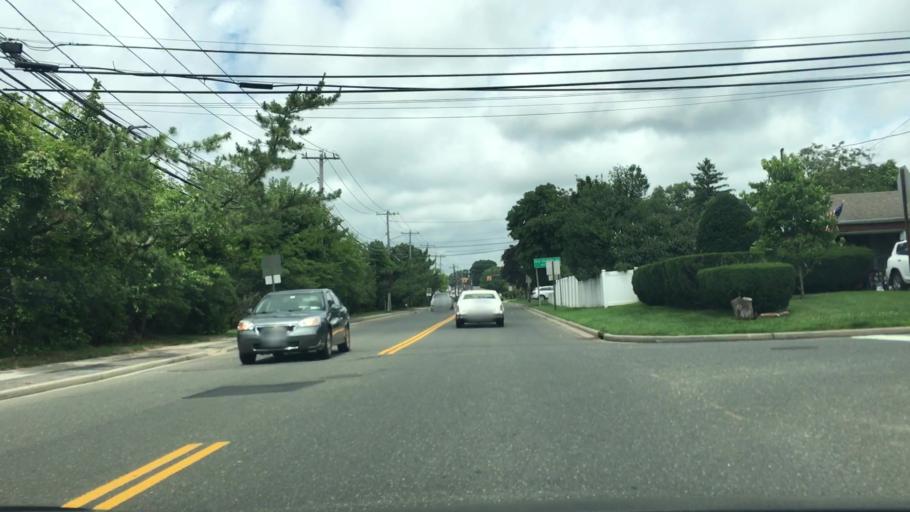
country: US
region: New York
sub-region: Nassau County
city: Hicksville
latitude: 40.7655
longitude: -73.5072
